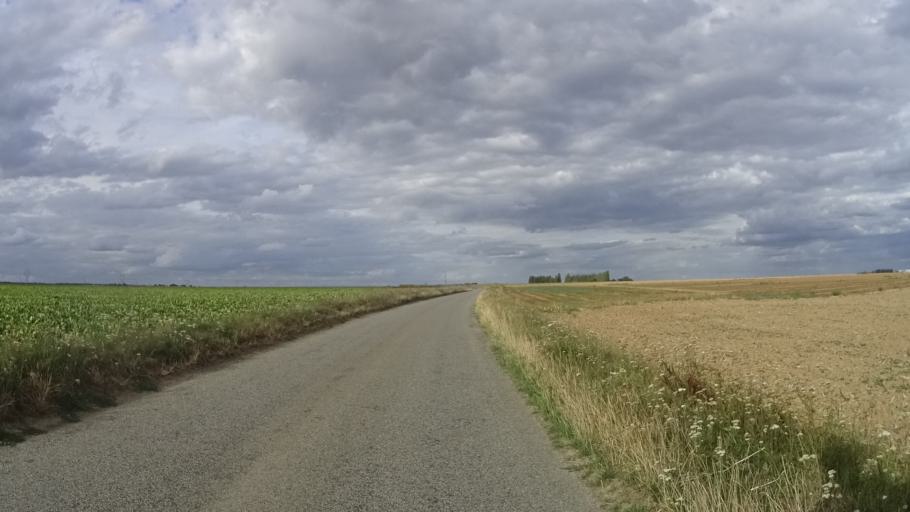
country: FR
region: Picardie
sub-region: Departement de l'Oise
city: Lagny-le-Sec
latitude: 49.1028
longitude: 2.7168
